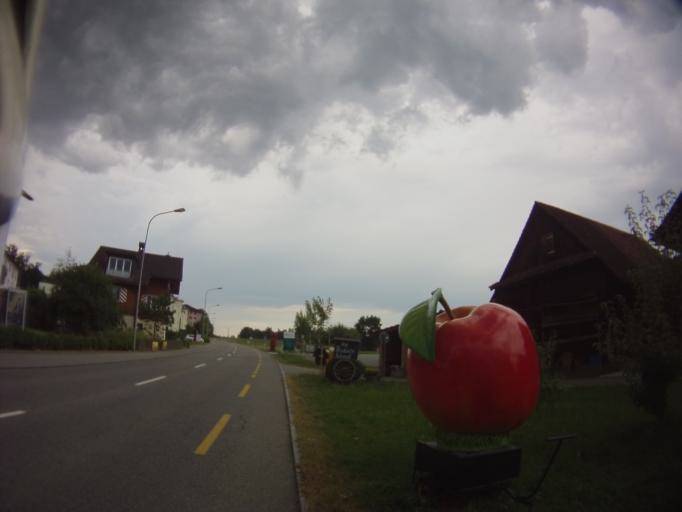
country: CH
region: Zug
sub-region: Zug
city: Cham
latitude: 47.1804
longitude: 8.4460
